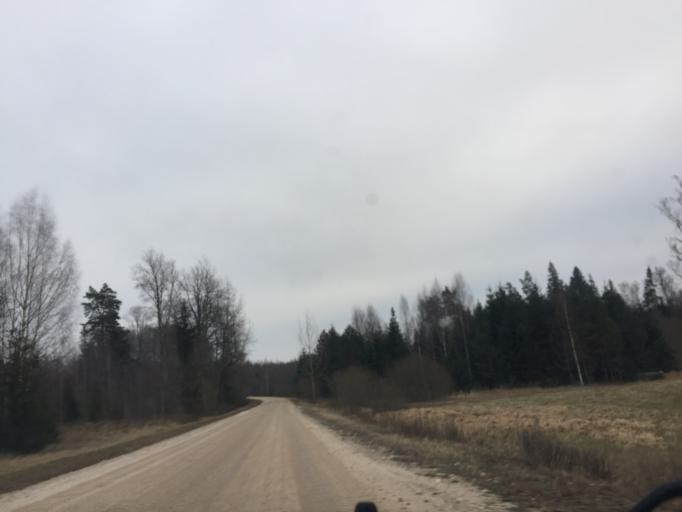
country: LV
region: Ligatne
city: Ligatne
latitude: 57.2112
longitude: 25.1336
